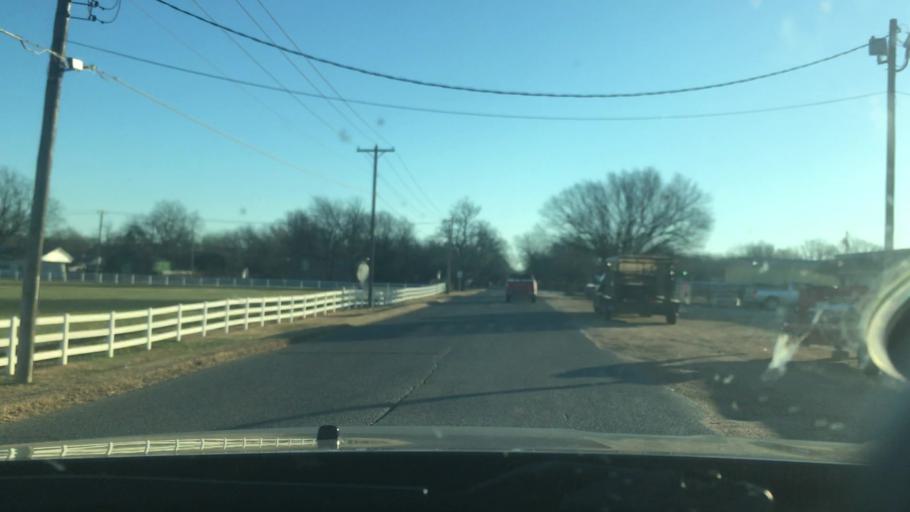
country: US
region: Oklahoma
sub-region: Pontotoc County
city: Ada
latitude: 34.7713
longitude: -96.6961
